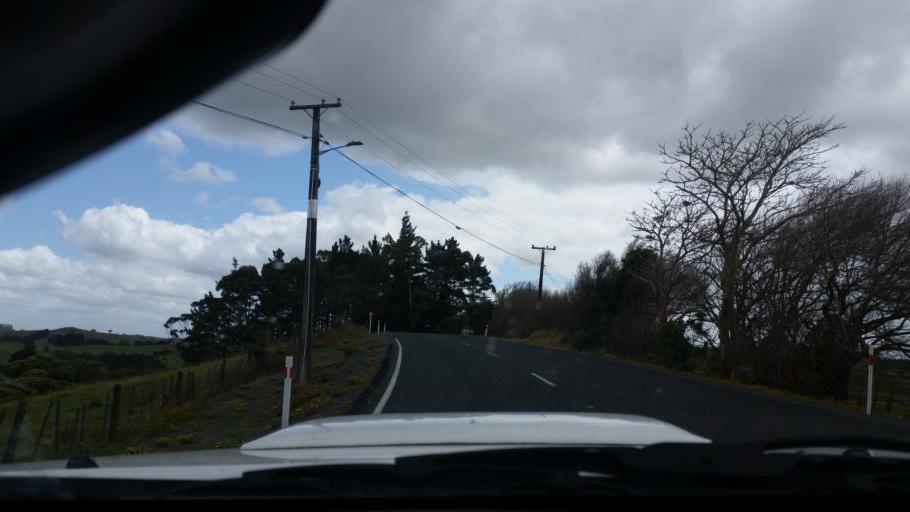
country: NZ
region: Northland
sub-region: Whangarei
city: Ruakaka
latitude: -36.1046
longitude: 174.3503
